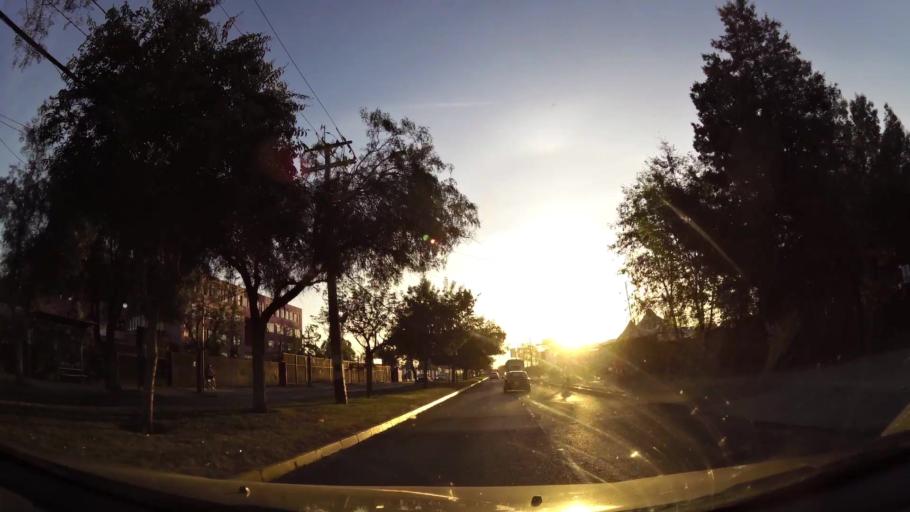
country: CL
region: Santiago Metropolitan
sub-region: Provincia de Cordillera
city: Puente Alto
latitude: -33.5978
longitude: -70.5747
